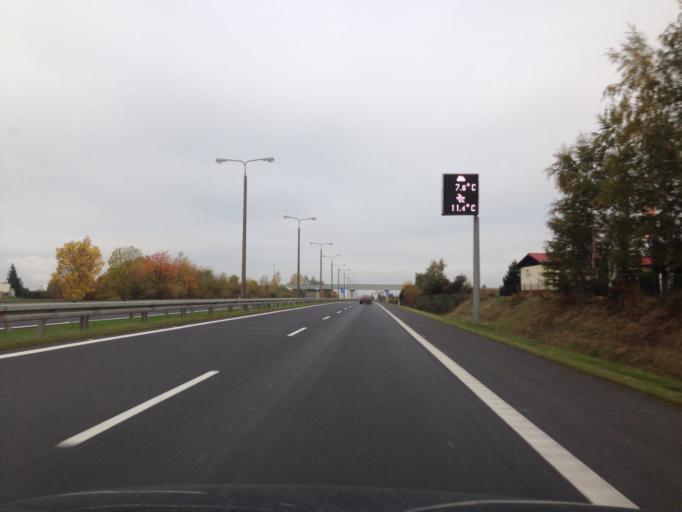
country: PL
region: Kujawsko-Pomorskie
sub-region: Powiat swiecki
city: Swiecie
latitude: 53.4203
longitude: 18.4726
